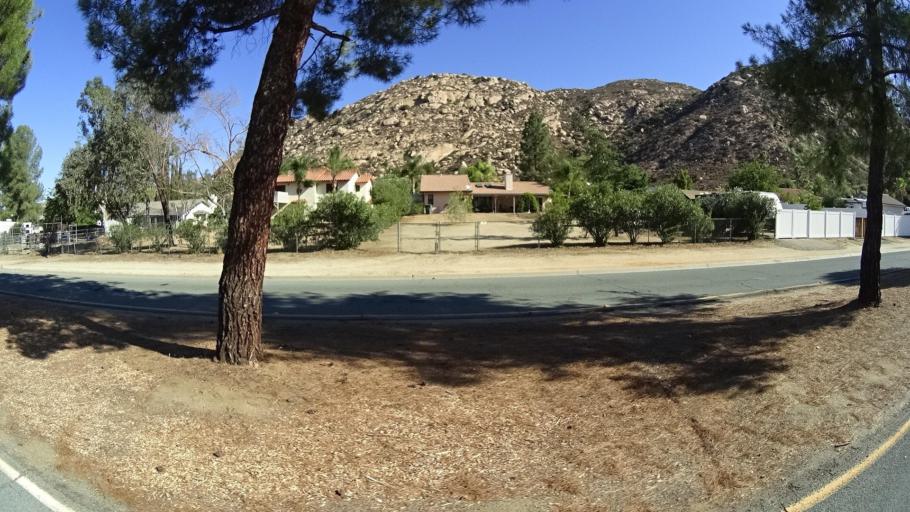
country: US
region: California
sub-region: San Diego County
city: San Diego Country Estates
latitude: 33.0056
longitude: -116.7815
